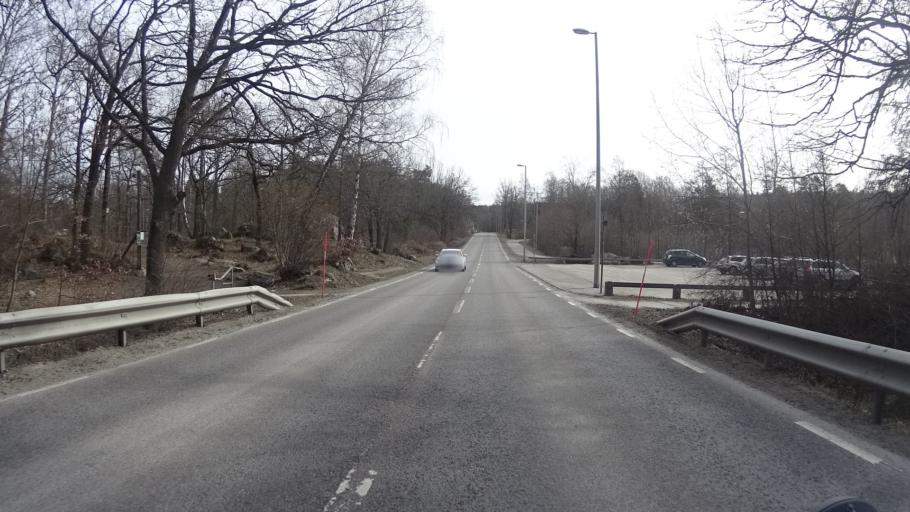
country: SE
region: Stockholm
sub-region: Nacka Kommun
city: Nacka
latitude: 59.2906
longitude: 18.1541
